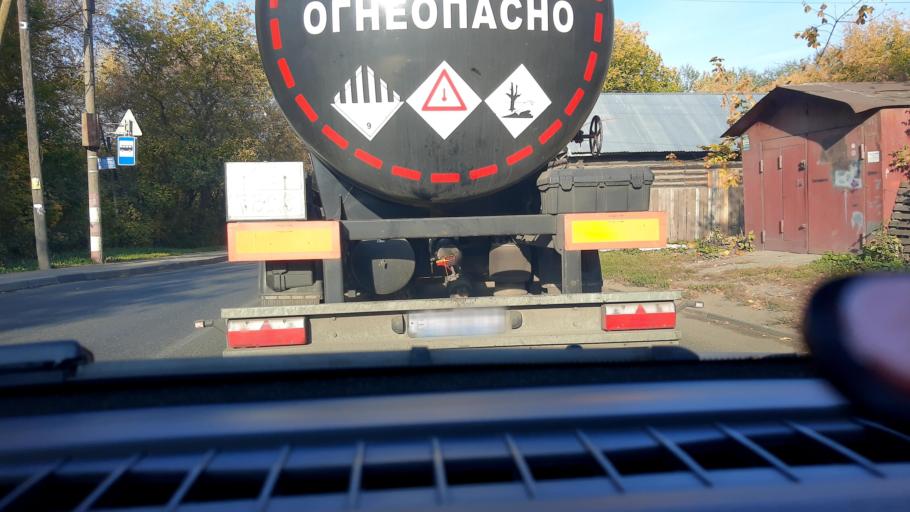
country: RU
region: Nizjnij Novgorod
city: Nizhniy Novgorod
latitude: 56.2825
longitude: 43.9547
